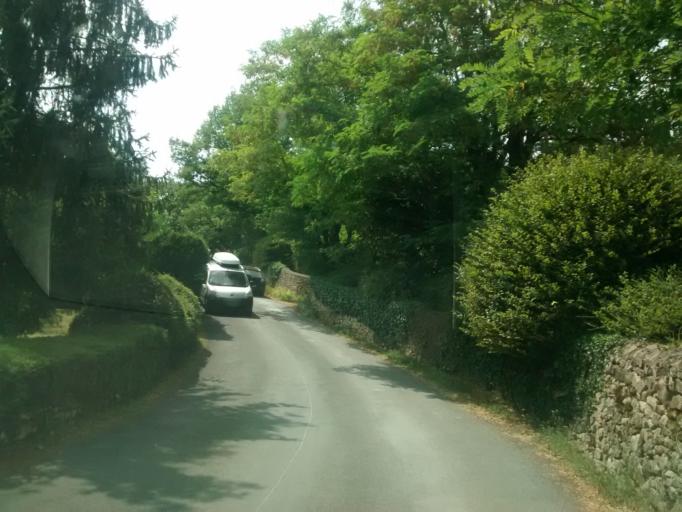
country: FR
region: Aquitaine
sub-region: Departement de la Dordogne
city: Cenac-et-Saint-Julien
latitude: 44.8162
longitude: 1.1424
